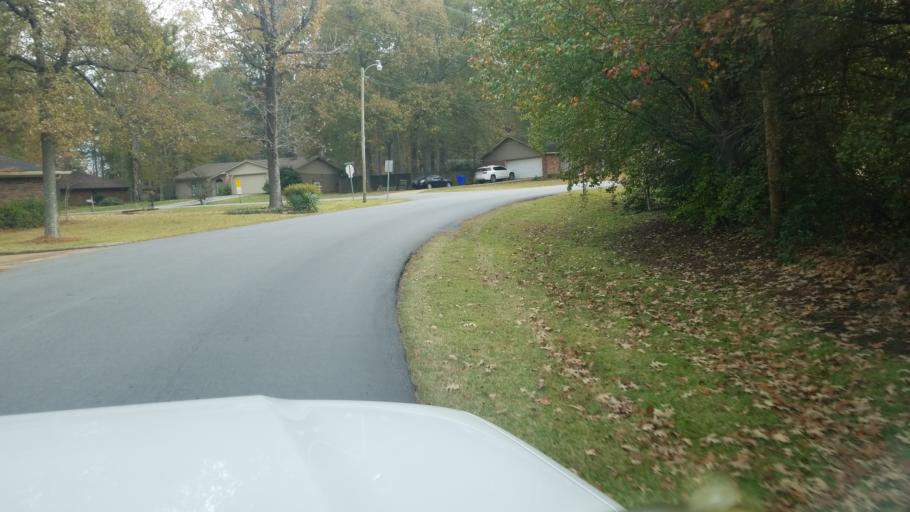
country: US
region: Mississippi
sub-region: Madison County
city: Ridgeland
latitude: 32.3813
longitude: -90.0319
